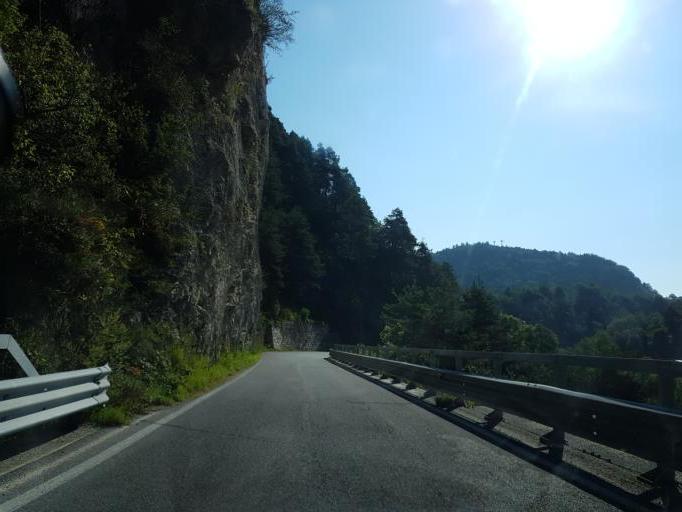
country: IT
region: Piedmont
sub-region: Provincia di Cuneo
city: San Damiano Macra
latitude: 44.4925
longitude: 7.2336
